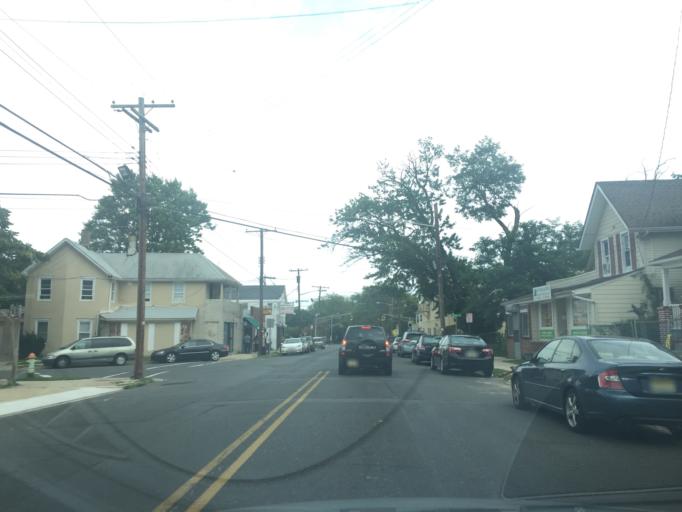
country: US
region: New Jersey
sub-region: Monmouth County
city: Asbury Park
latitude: 40.2222
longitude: -74.0206
